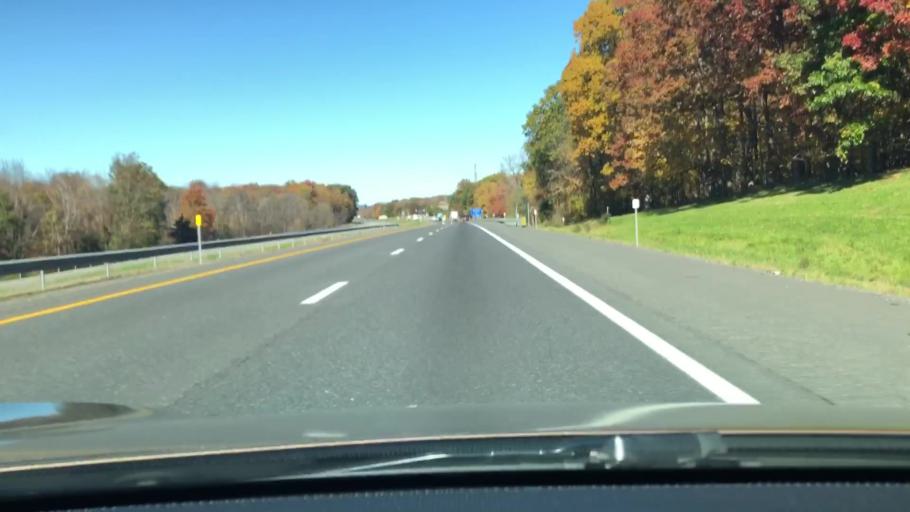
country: US
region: New York
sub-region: Orange County
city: Orange Lake
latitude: 41.5702
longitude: -74.0840
